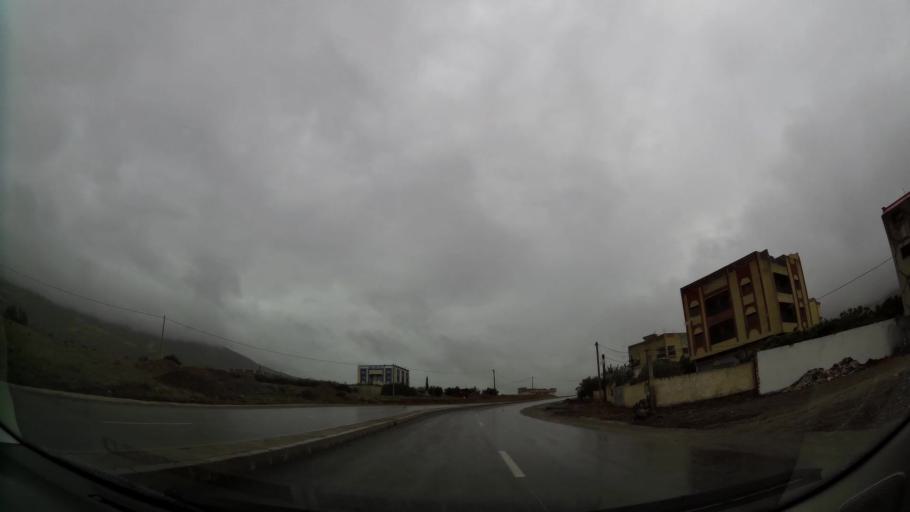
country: MA
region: Taza-Al Hoceima-Taounate
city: Imzourene
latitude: 35.0383
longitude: -3.8211
